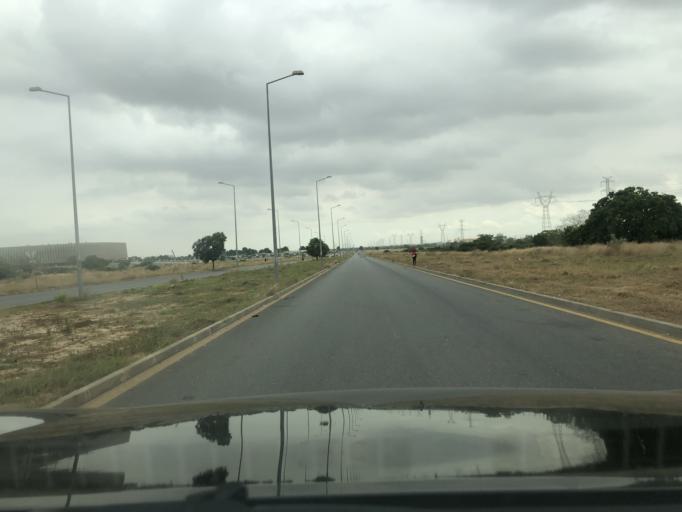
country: AO
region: Luanda
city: Luanda
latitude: -8.9757
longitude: 13.2875
